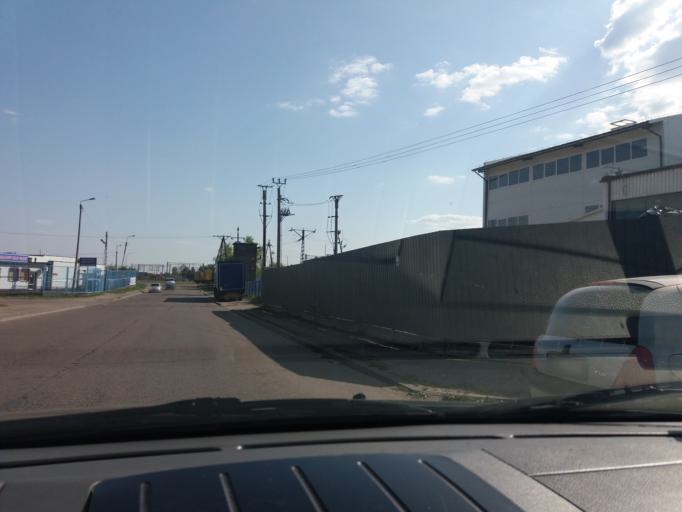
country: PL
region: Masovian Voivodeship
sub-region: Powiat mlawski
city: Mlawa
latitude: 53.1177
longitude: 20.3589
